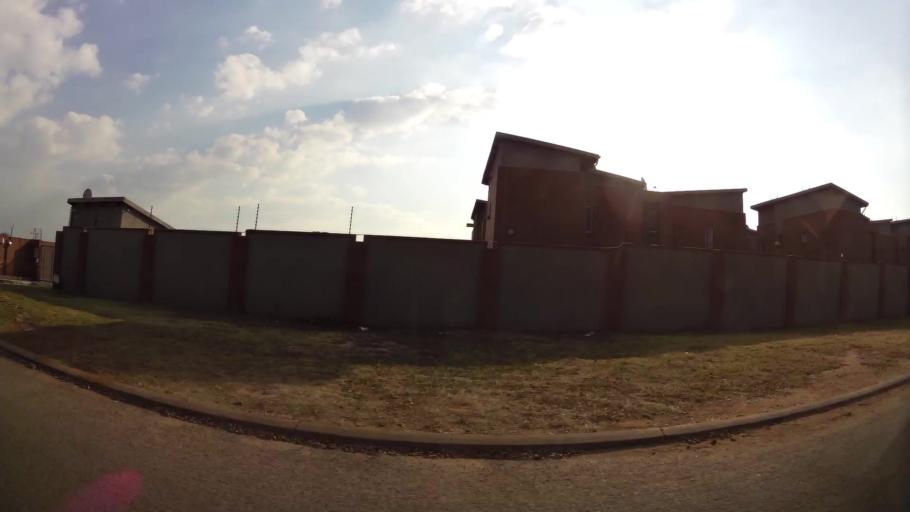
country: ZA
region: Gauteng
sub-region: City of Johannesburg Metropolitan Municipality
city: Modderfontein
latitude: -26.0959
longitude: 28.1948
